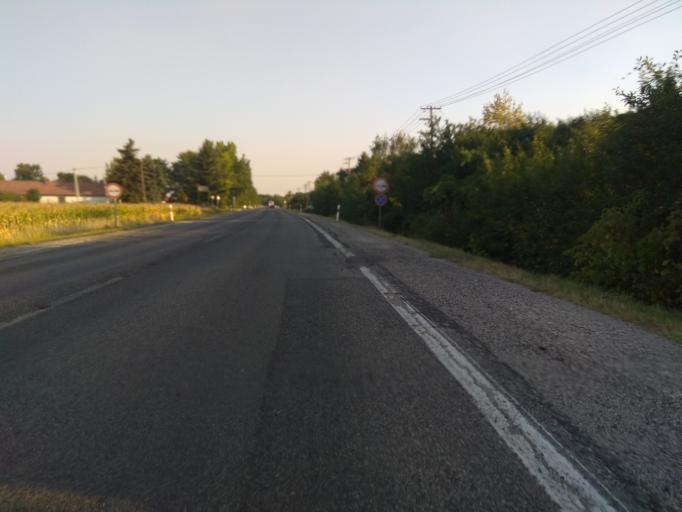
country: HU
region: Borsod-Abauj-Zemplen
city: Nyekladhaza
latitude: 47.9745
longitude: 20.8301
